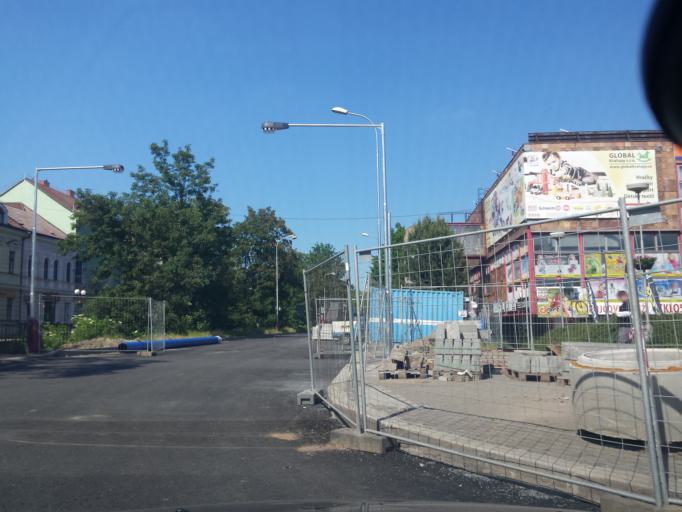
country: CZ
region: Central Bohemia
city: Kralupy nad Vltavou
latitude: 50.2408
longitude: 14.3096
